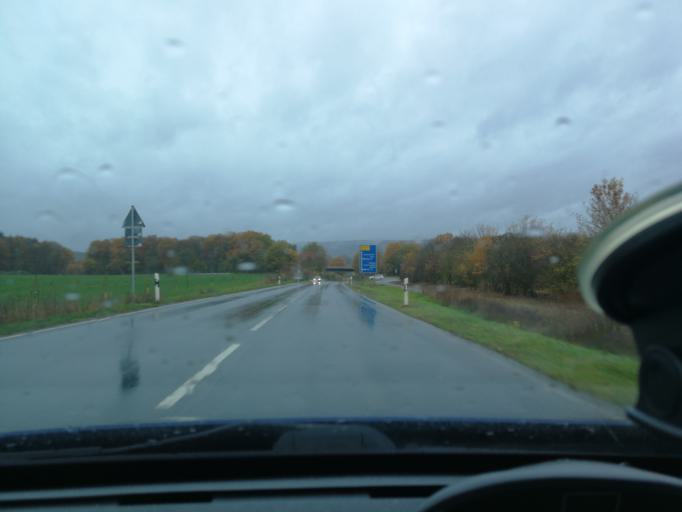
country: DE
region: Rheinland-Pfalz
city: Esch
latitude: 49.9017
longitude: 6.8602
